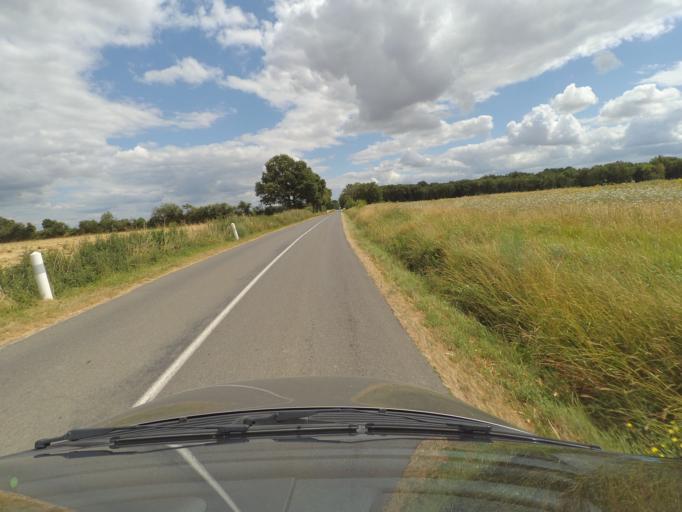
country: FR
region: Poitou-Charentes
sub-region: Departement de la Vienne
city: Saint-Savin
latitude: 46.5595
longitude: 0.9387
